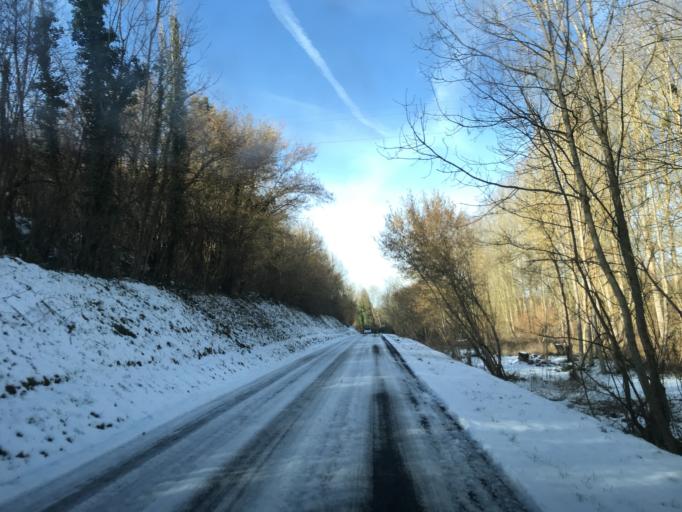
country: FR
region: Haute-Normandie
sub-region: Departement de l'Eure
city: Saint-Aubin-sur-Gaillon
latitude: 49.0802
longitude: 1.2796
